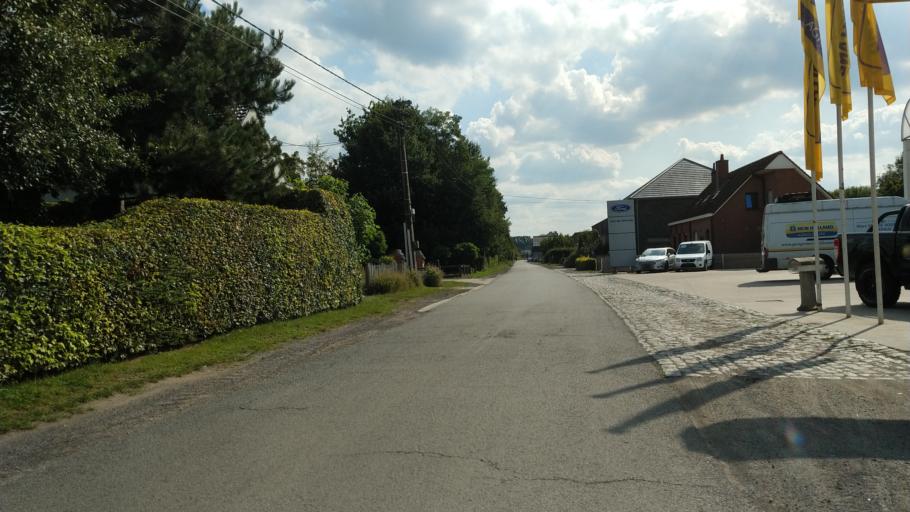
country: BE
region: Flanders
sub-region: Provincie Oost-Vlaanderen
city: Kaprijke
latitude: 51.1947
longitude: 3.6798
